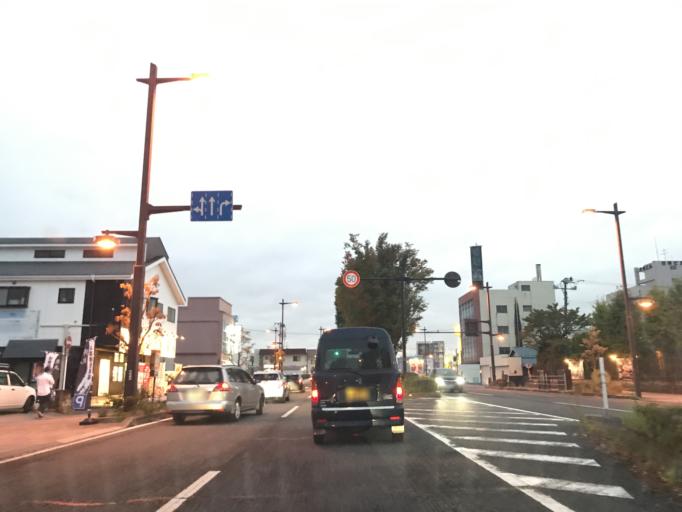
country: JP
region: Fukushima
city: Koriyama
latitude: 37.3883
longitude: 140.3817
